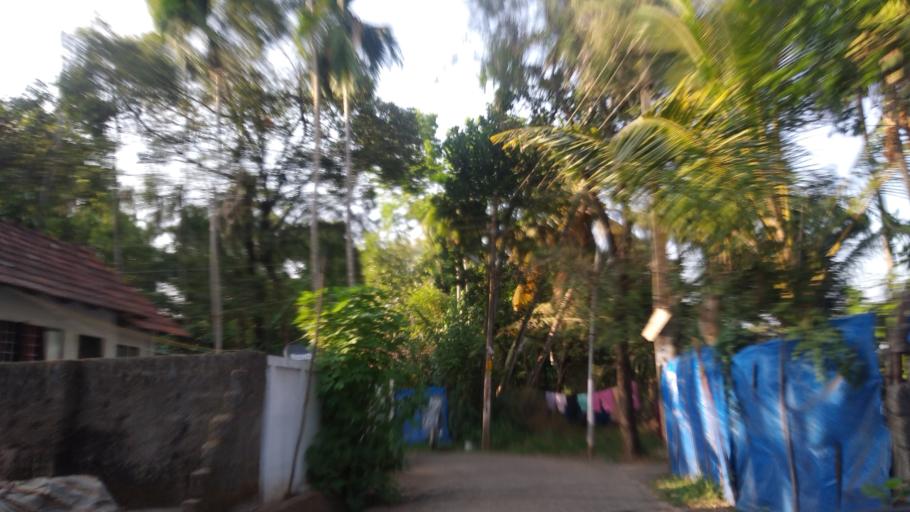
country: IN
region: Kerala
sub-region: Thrissur District
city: Kodungallur
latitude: 10.1296
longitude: 76.2044
